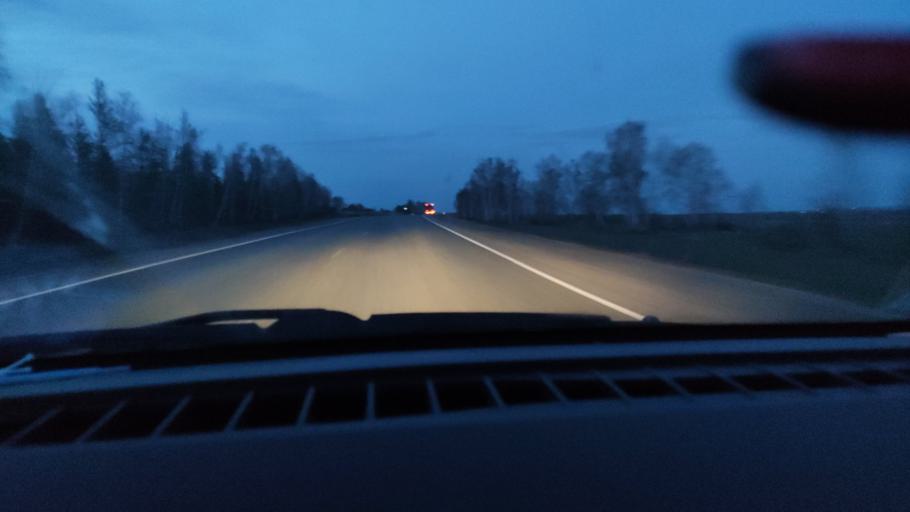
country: RU
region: Saratov
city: Sennoy
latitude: 52.1348
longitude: 46.8695
